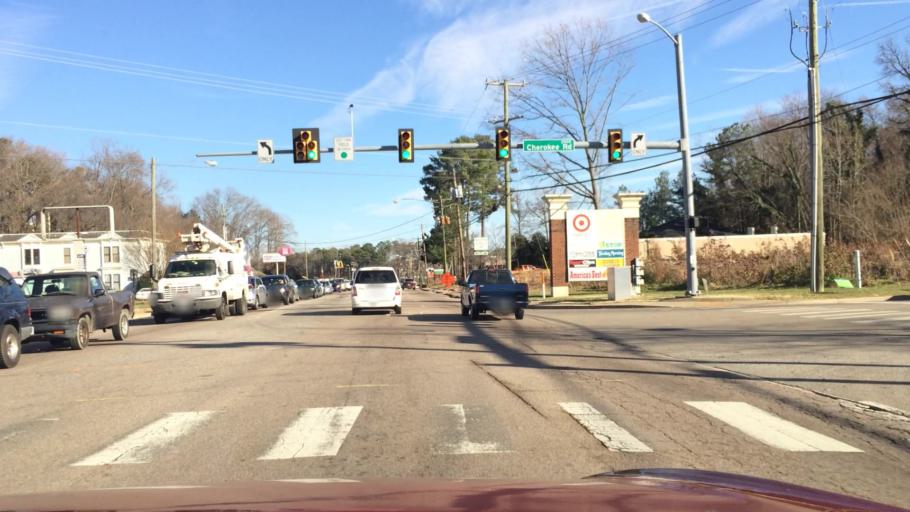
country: US
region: Virginia
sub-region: Chesterfield County
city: Bon Air
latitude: 37.5373
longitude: -77.5241
